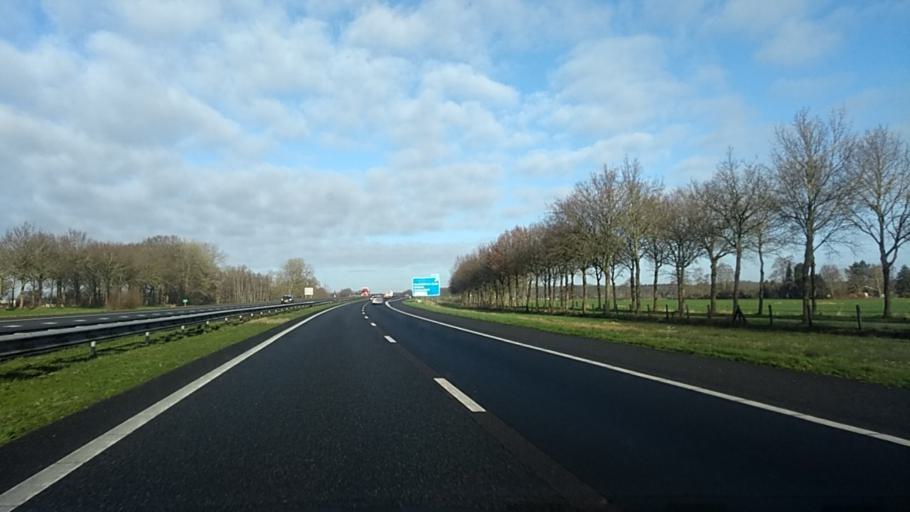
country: NL
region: Friesland
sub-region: Gemeente Heerenveen
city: Oudeschoot
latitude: 52.9246
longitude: 5.9651
